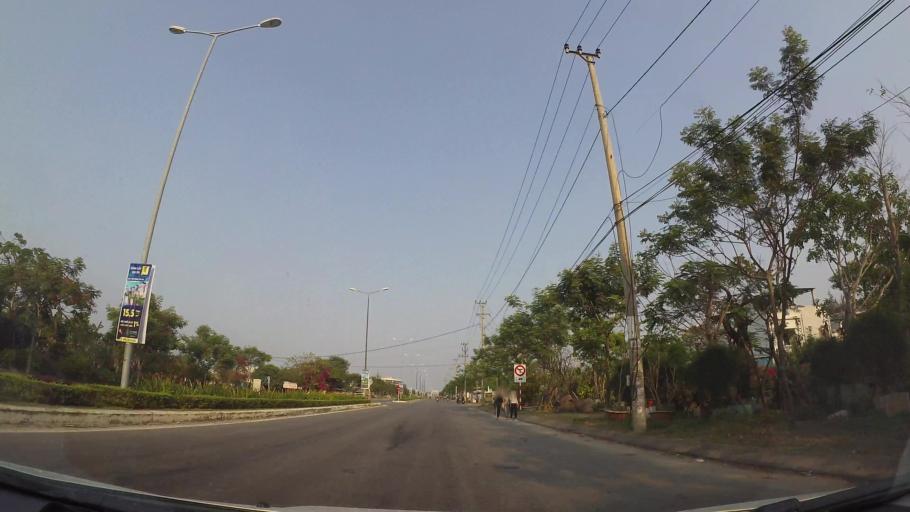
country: VN
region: Da Nang
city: Ngu Hanh Son
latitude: 15.9779
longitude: 108.2560
